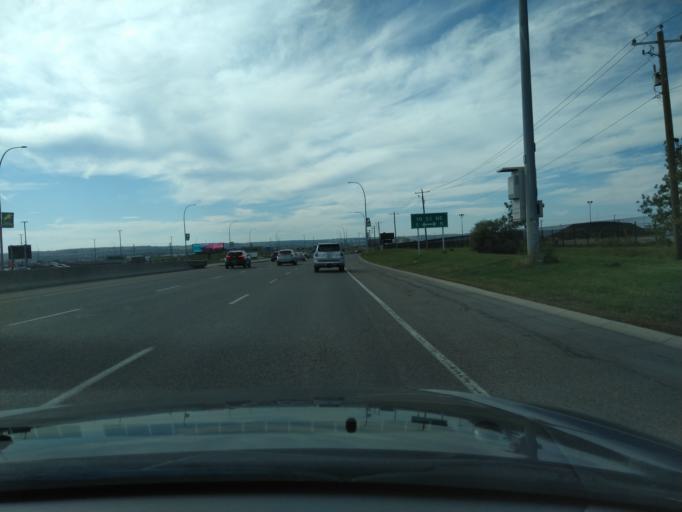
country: CA
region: Alberta
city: Calgary
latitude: 51.1396
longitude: -114.0088
